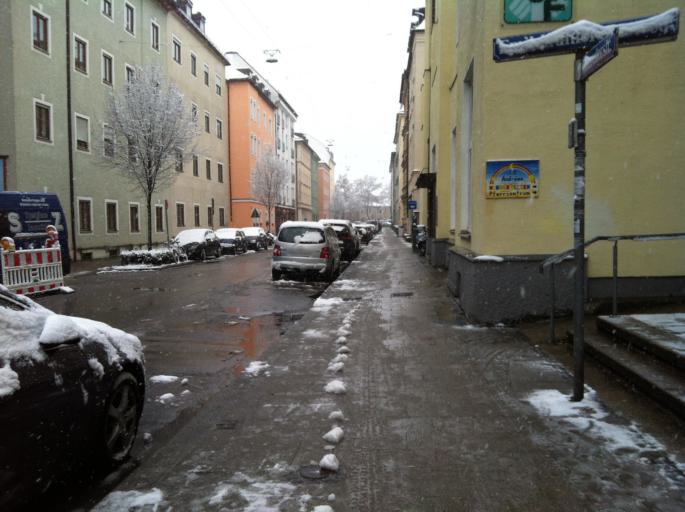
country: DE
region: Bavaria
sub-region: Upper Bavaria
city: Munich
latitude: 48.1262
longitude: 11.5558
